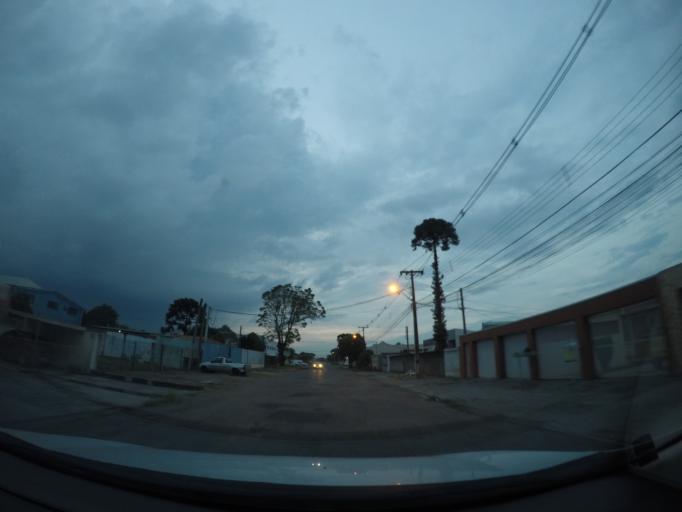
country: BR
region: Parana
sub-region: Sao Jose Dos Pinhais
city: Sao Jose dos Pinhais
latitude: -25.4961
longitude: -49.2319
